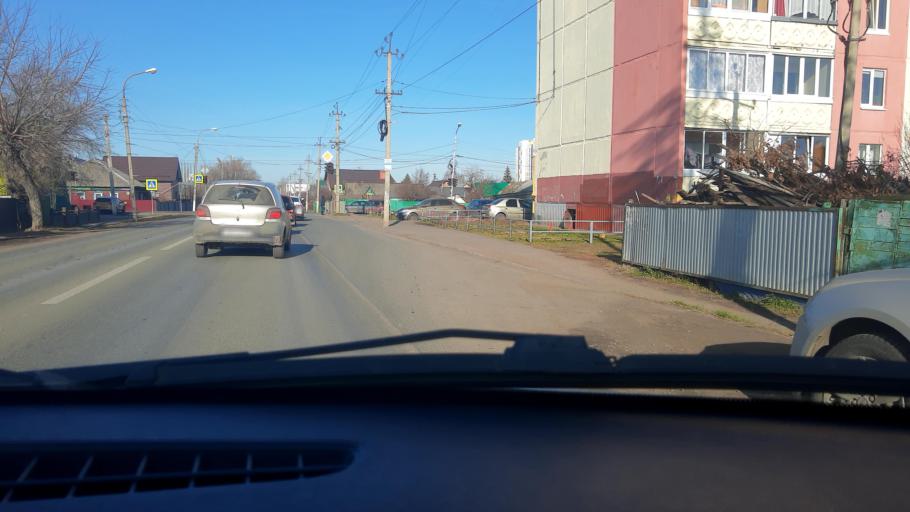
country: RU
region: Bashkortostan
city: Avdon
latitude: 54.7076
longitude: 55.8198
